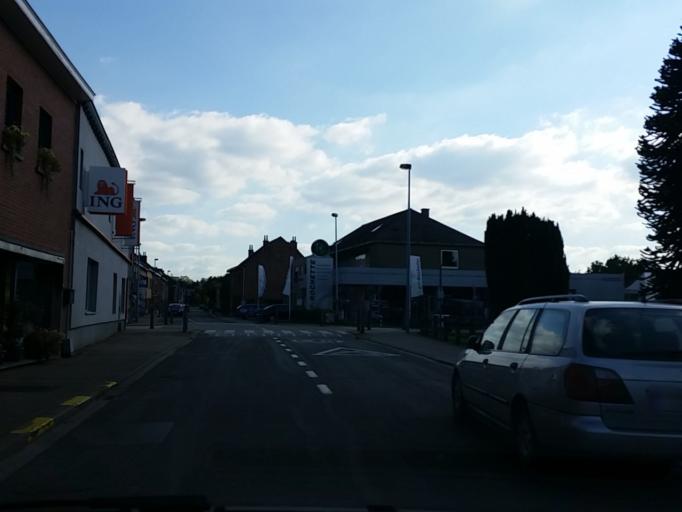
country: BE
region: Flanders
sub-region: Provincie Vlaams-Brabant
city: Bertem
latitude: 50.9039
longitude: 4.6212
